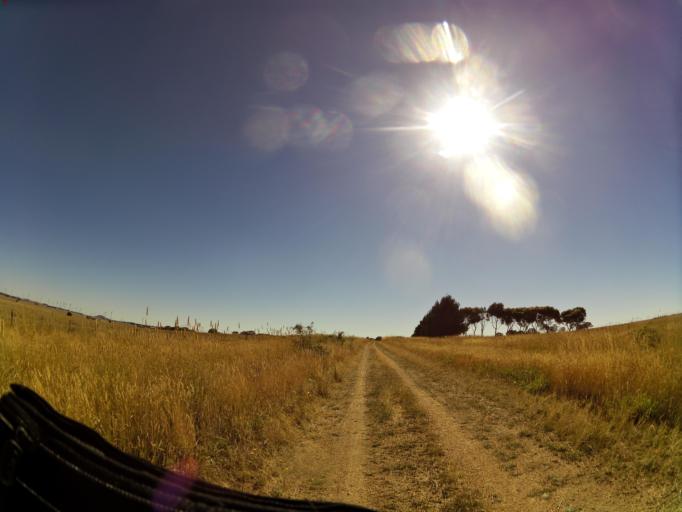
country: AU
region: Victoria
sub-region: Ballarat North
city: Delacombe
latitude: -37.6876
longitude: 143.3901
